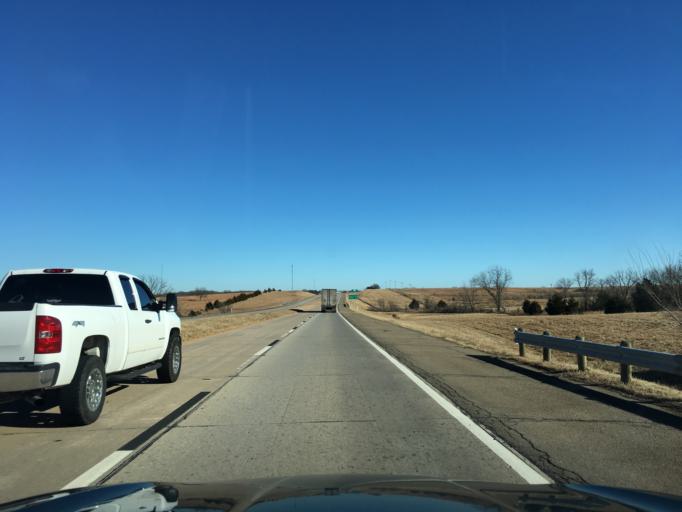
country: US
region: Oklahoma
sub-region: Pawnee County
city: Pawnee
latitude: 36.2248
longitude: -96.7687
